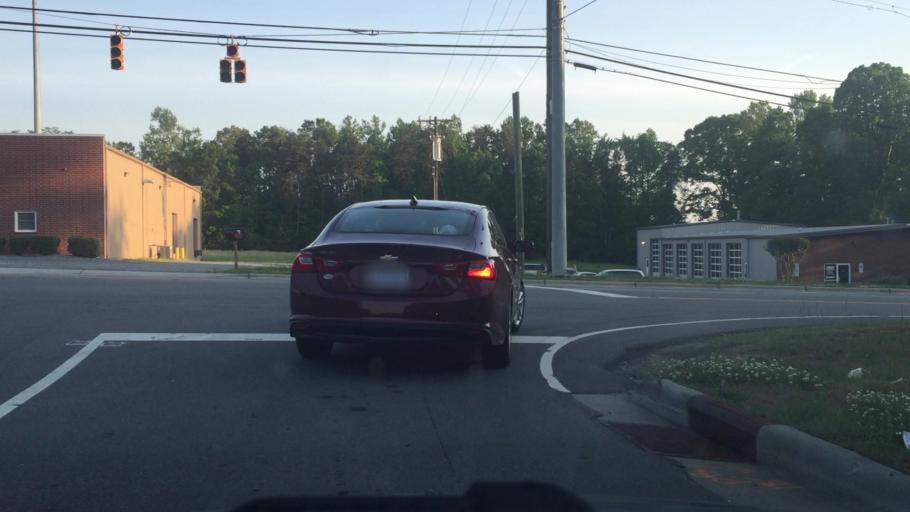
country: US
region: North Carolina
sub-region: Rockingham County
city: Reidsville
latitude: 36.3340
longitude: -79.6956
